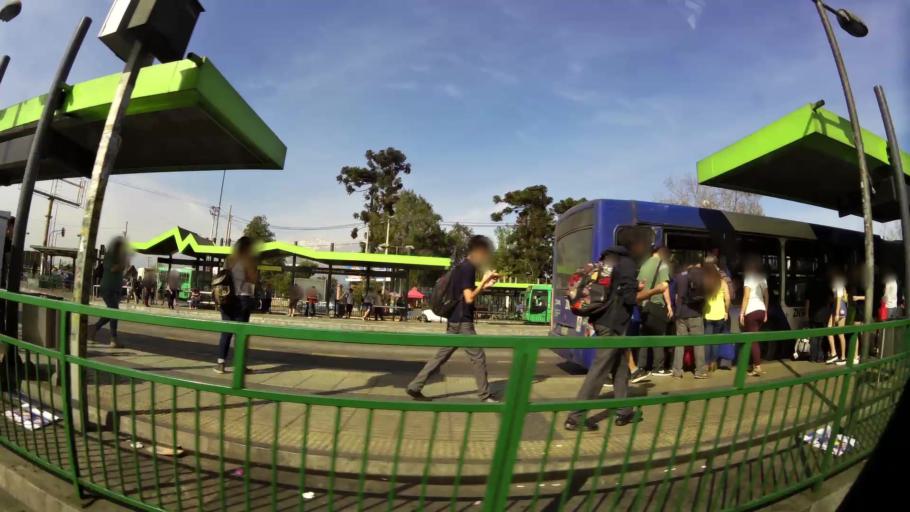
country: CL
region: Santiago Metropolitan
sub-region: Provincia de Santiago
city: La Pintana
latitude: -33.5432
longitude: -70.6342
